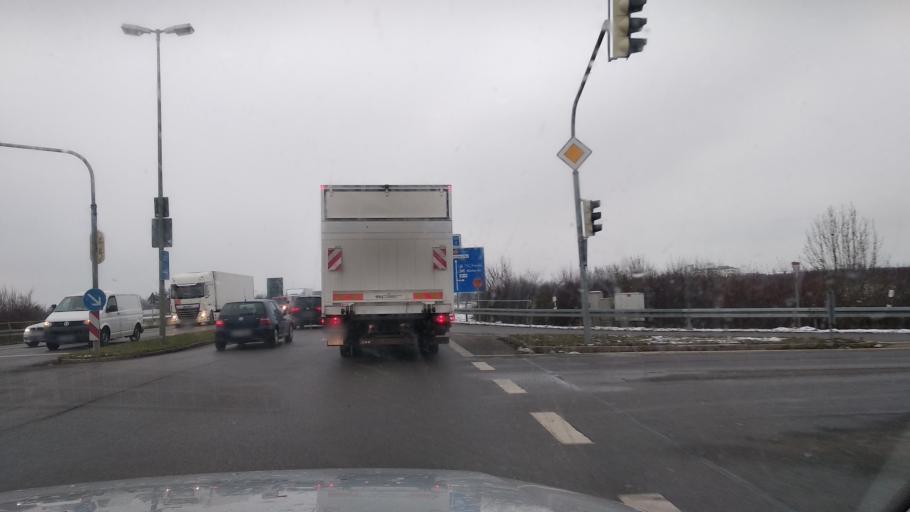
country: DE
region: Bavaria
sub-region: Upper Bavaria
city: Feldkirchen
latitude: 48.1462
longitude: 11.7457
